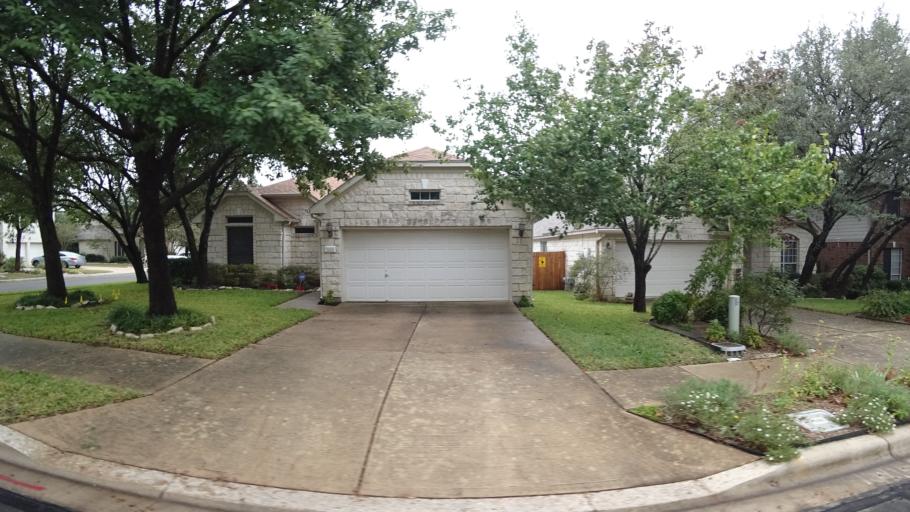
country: US
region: Texas
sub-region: Travis County
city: Shady Hollow
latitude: 30.1892
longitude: -97.8675
